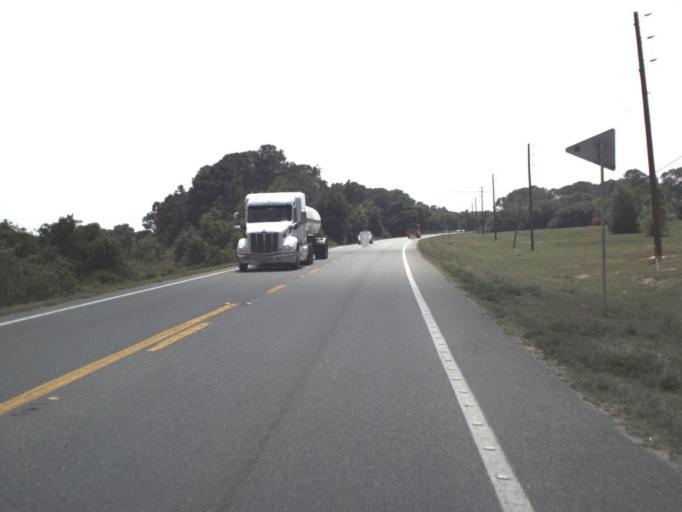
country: US
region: Florida
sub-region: Lake County
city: Howie In The Hills
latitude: 28.6667
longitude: -81.7814
